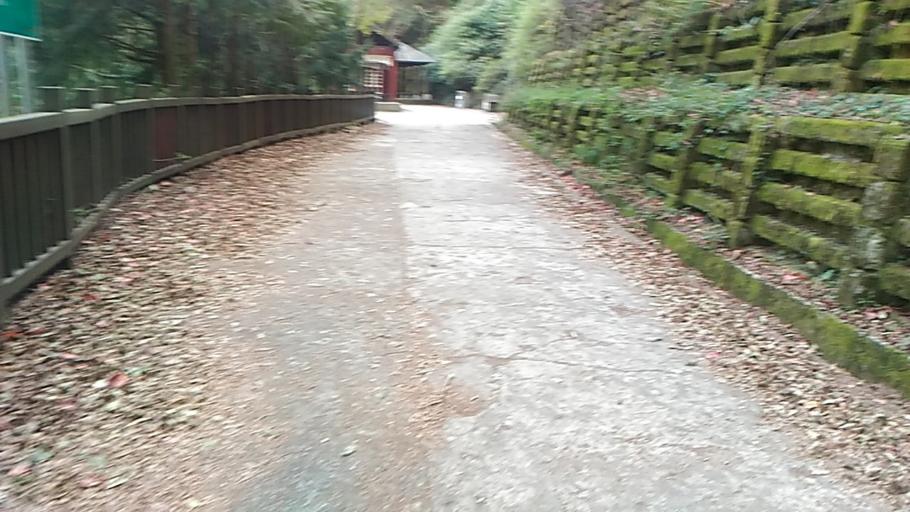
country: TW
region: Taiwan
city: Daxi
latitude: 24.4130
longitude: 121.3026
